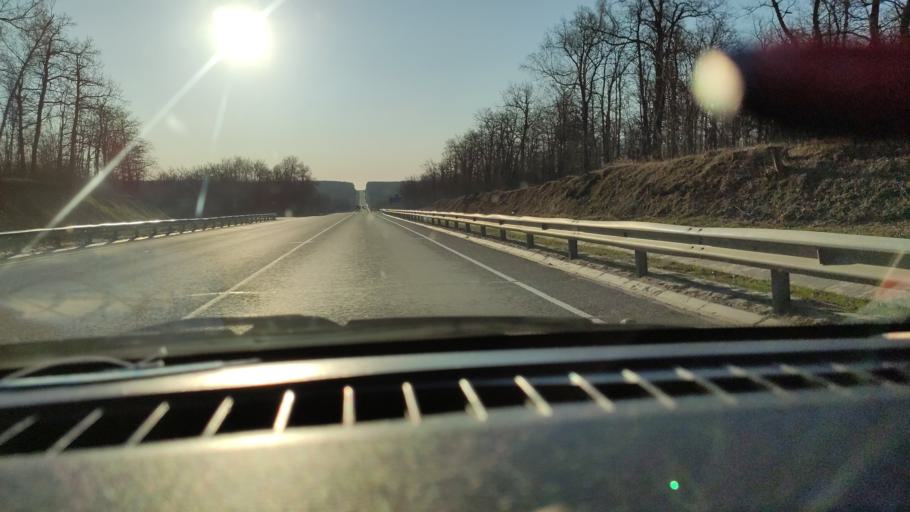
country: RU
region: Saratov
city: Vol'sk
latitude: 52.1095
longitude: 47.3747
